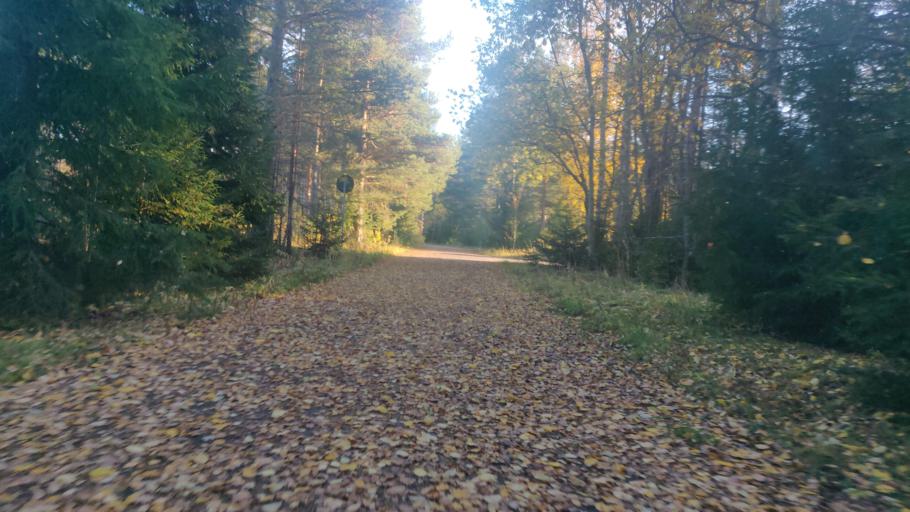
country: SE
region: Vaesternorrland
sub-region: Sundsvalls Kommun
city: Njurundabommen
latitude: 62.2695
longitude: 17.3981
